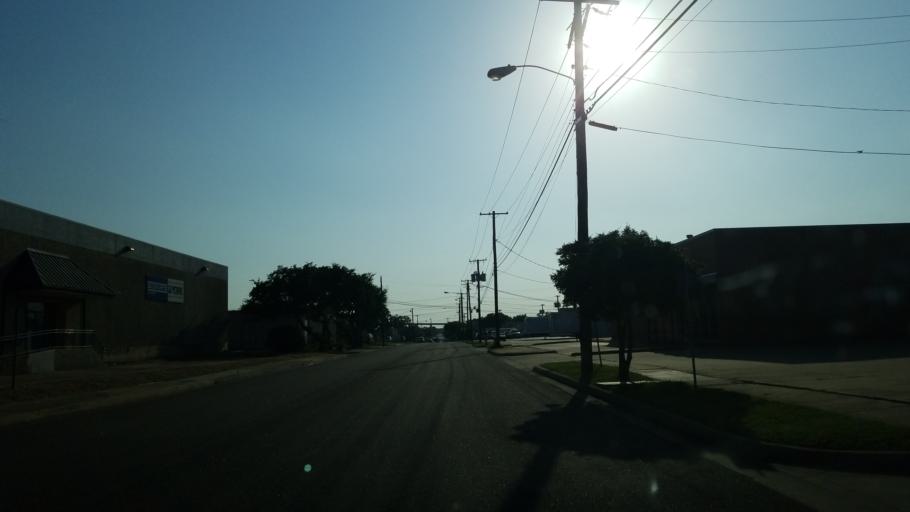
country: US
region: Texas
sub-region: Dallas County
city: Farmers Branch
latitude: 32.8739
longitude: -96.8869
